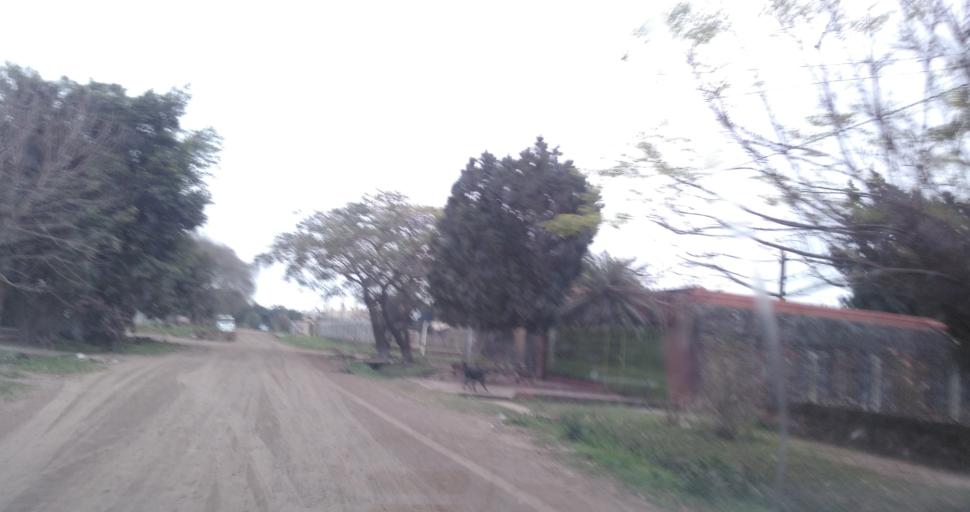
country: AR
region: Chaco
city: Fontana
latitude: -27.4357
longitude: -59.0166
